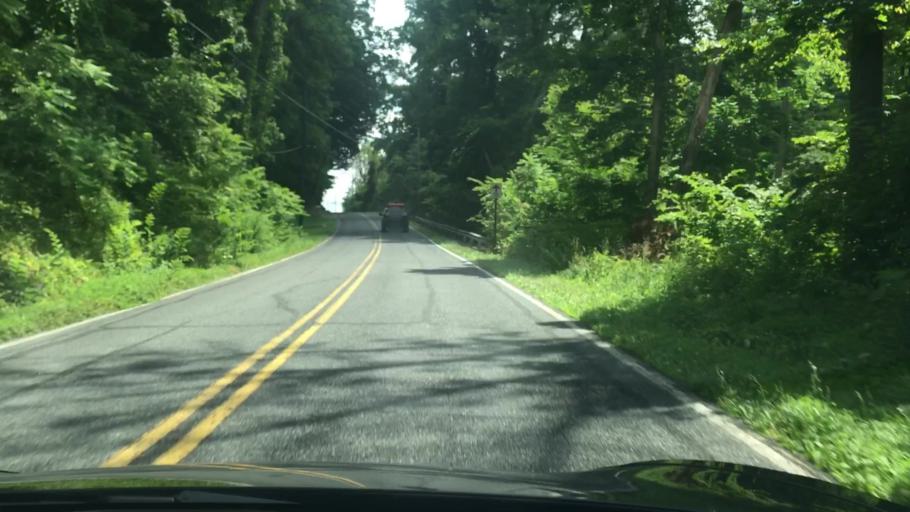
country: US
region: Pennsylvania
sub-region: York County
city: Valley Green
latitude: 40.1240
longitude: -76.7852
